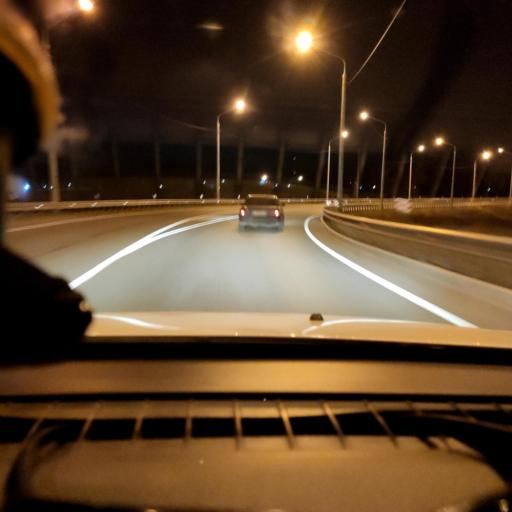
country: RU
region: Samara
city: Volzhskiy
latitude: 53.4341
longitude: 50.1143
